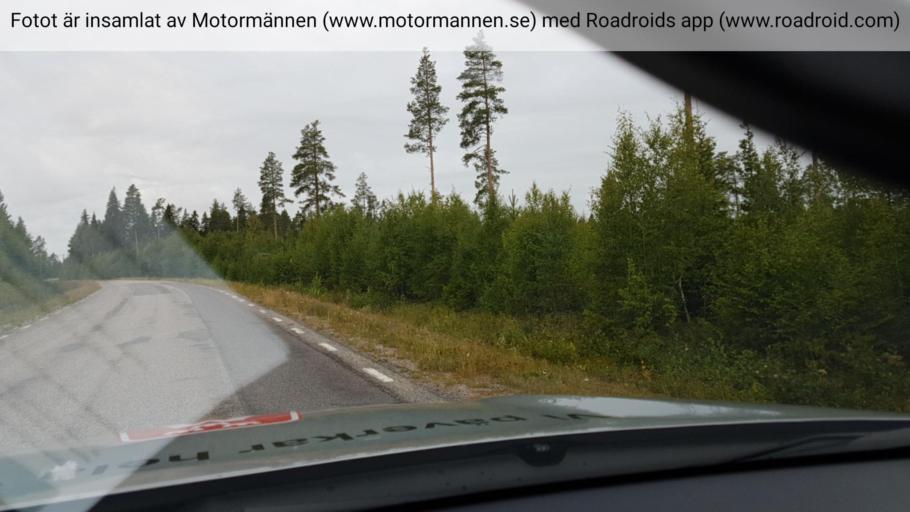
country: SE
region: Norrbotten
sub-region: Bodens Kommun
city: Saevast
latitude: 65.6671
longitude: 21.7554
